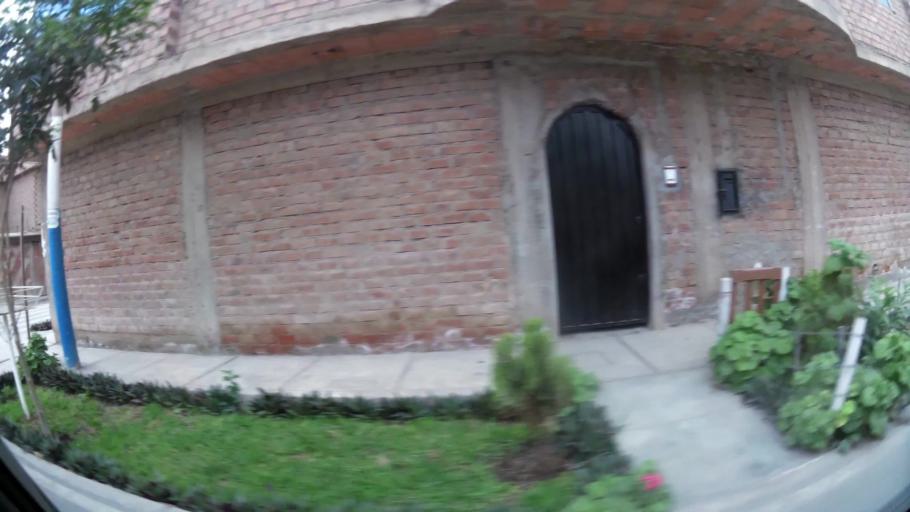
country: PE
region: Lima
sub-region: Lima
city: Independencia
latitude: -11.9744
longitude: -77.0957
